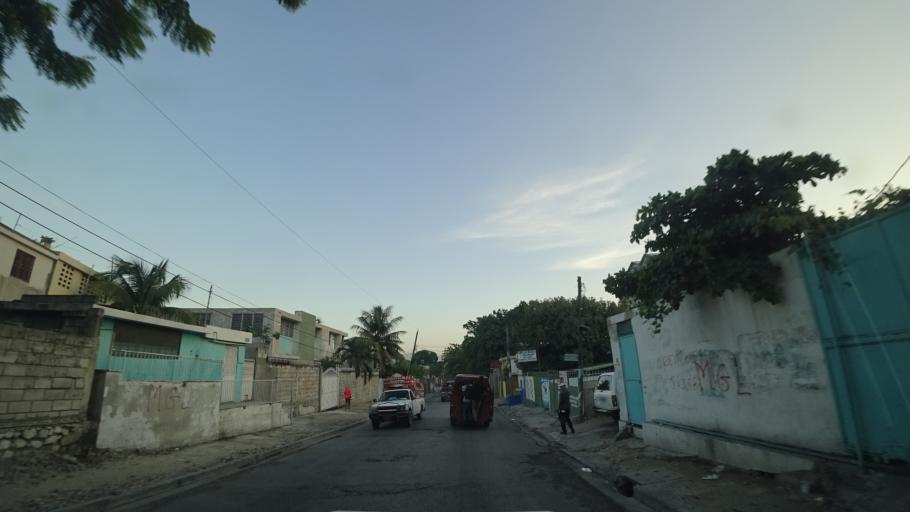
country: HT
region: Ouest
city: Delmas 73
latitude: 18.5521
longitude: -72.3056
